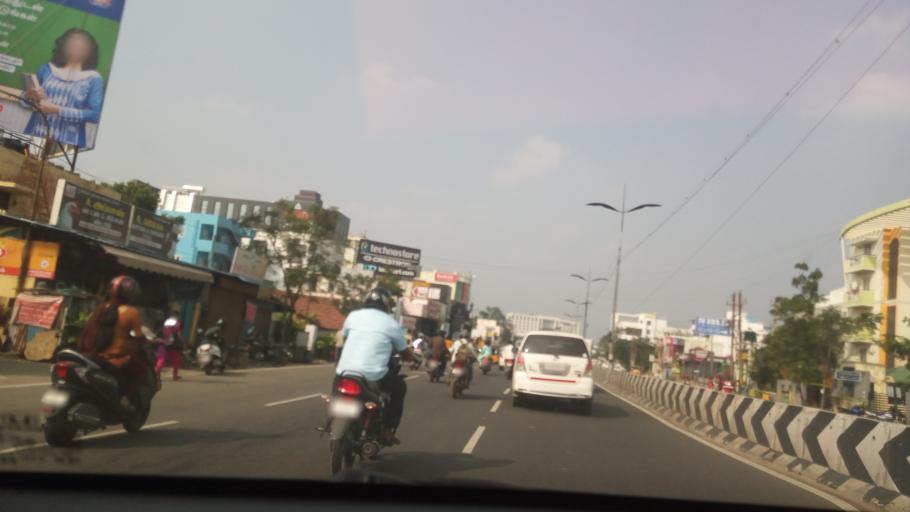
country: IN
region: Tamil Nadu
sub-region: Coimbatore
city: Coimbatore
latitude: 11.0223
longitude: 76.9994
